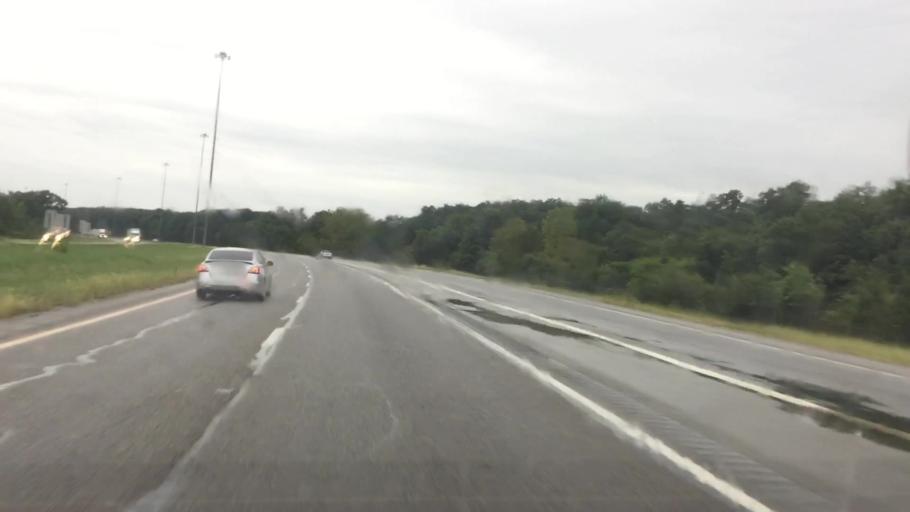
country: US
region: Ohio
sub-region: Defiance County
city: Defiance
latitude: 41.3083
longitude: -84.3559
